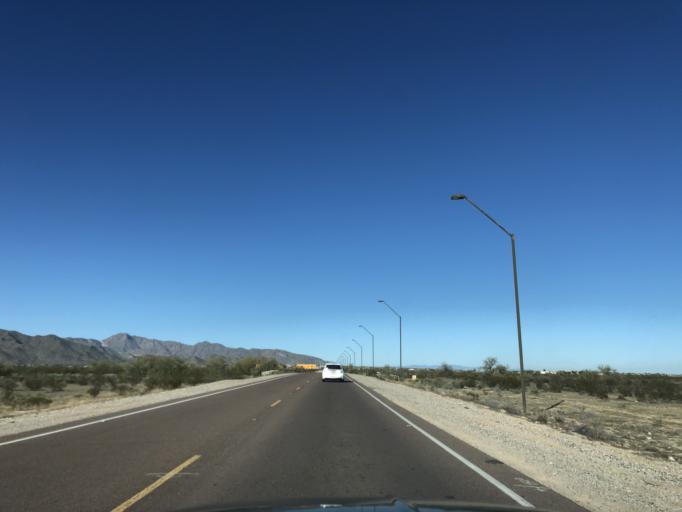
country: US
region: Arizona
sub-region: Maricopa County
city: Buckeye
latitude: 33.4397
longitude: -112.5042
